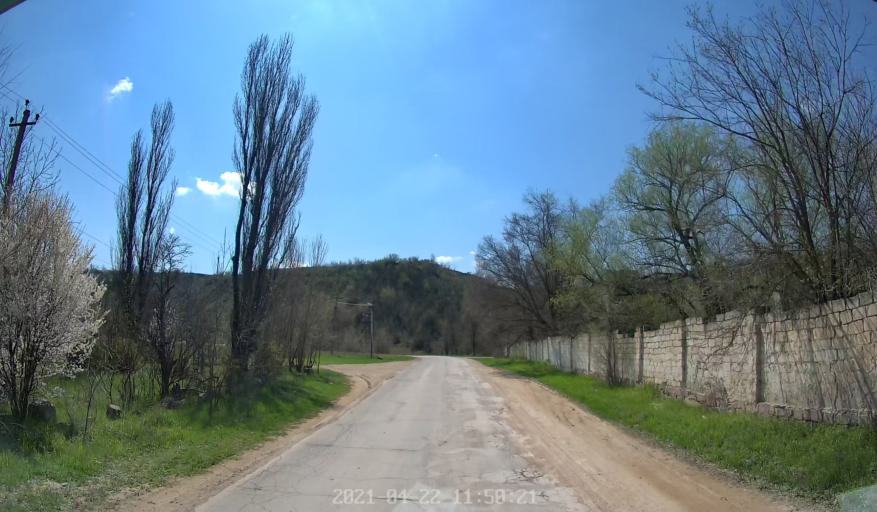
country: MD
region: Chisinau
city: Ciorescu
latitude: 47.1383
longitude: 28.8995
